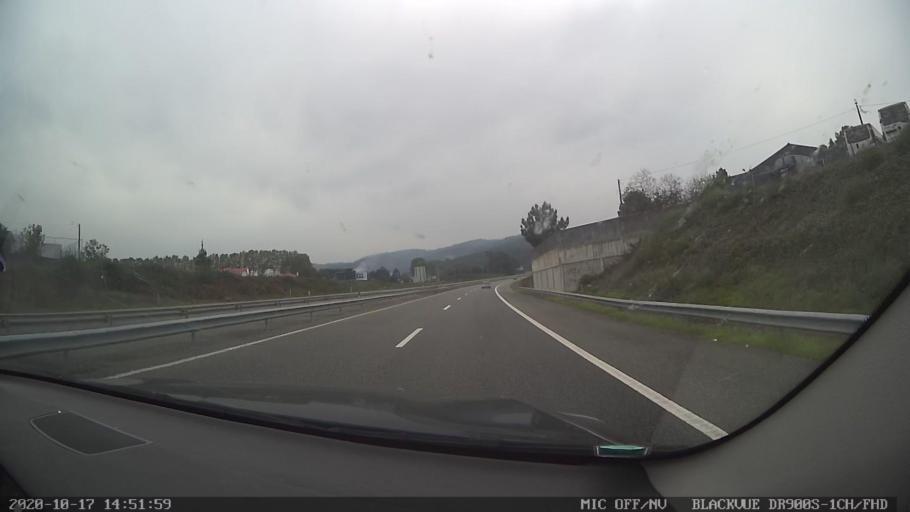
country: PT
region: Braga
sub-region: Barcelos
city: Barcelos
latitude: 41.5073
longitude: -8.6216
